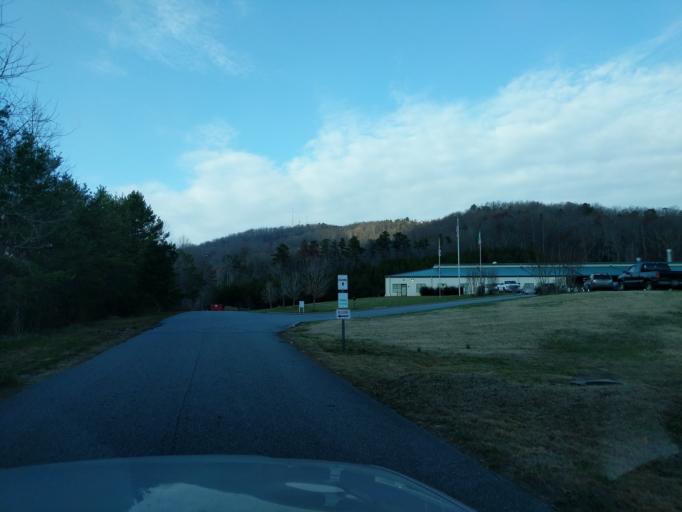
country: US
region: North Carolina
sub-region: McDowell County
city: West Marion
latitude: 35.6443
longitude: -81.9901
